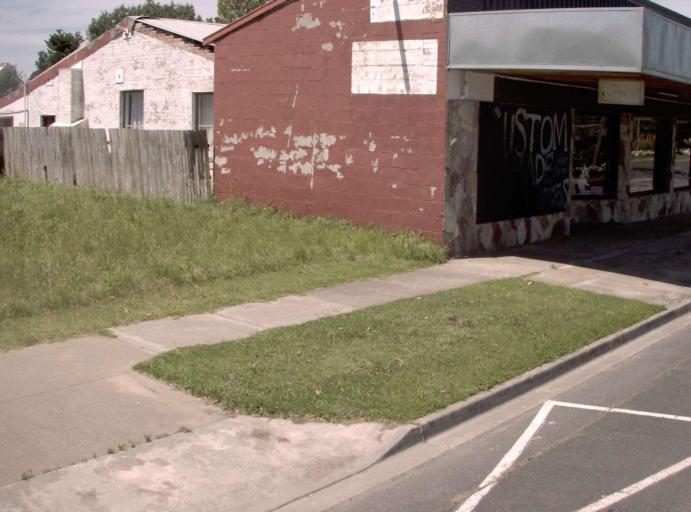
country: AU
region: Victoria
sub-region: Wellington
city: Heyfield
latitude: -38.1510
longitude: 146.7847
